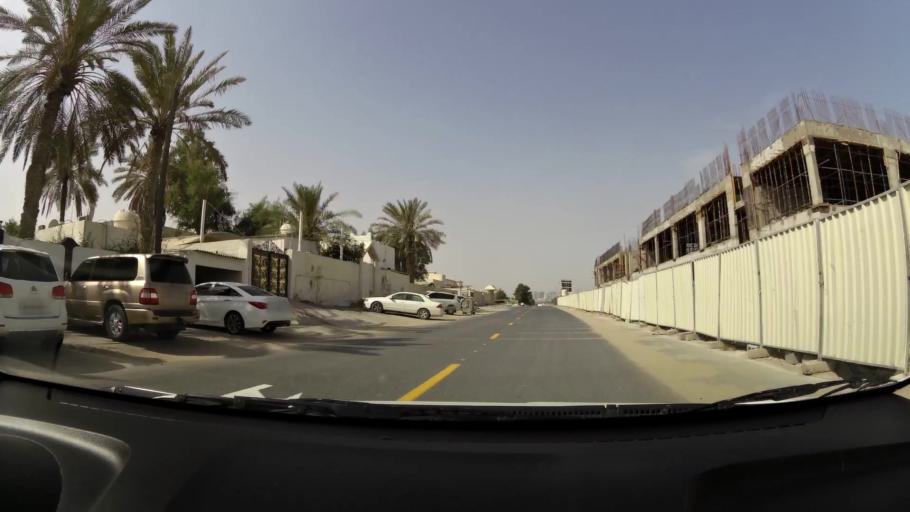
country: AE
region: Ash Shariqah
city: Sharjah
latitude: 25.3463
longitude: 55.4136
